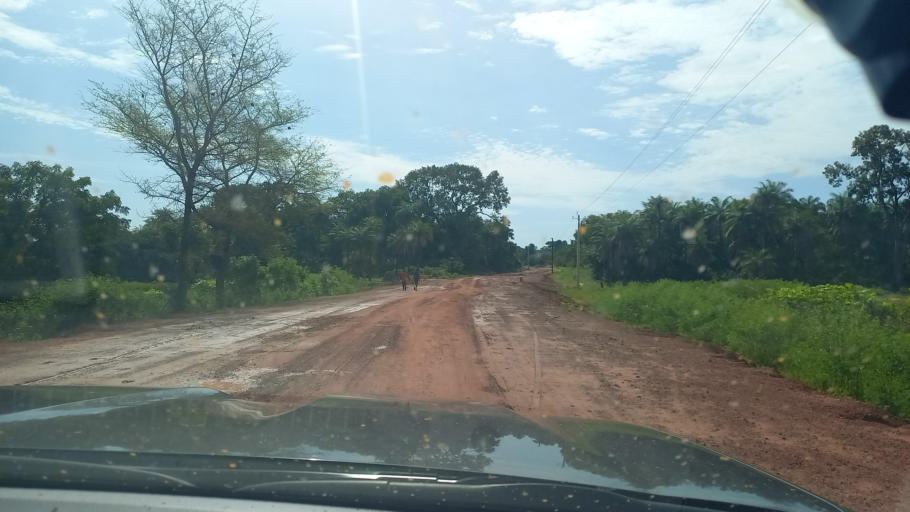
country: SN
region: Ziguinchor
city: Ziguinchor
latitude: 12.6729
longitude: -16.1915
